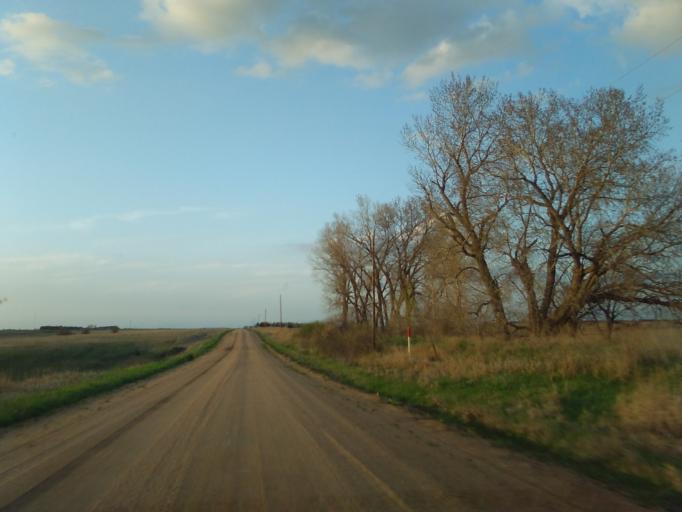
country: US
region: Nebraska
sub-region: Nuckolls County
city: Nelson
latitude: 40.2000
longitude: -98.2925
